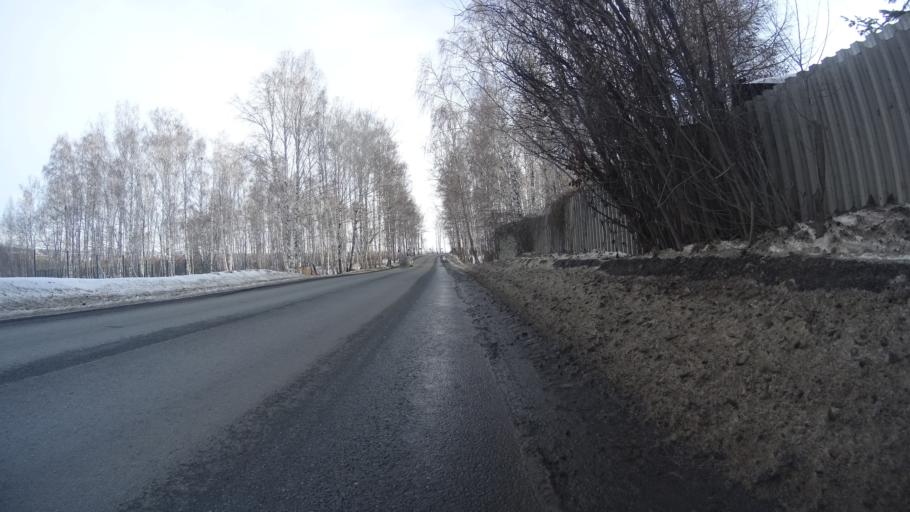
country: RU
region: Chelyabinsk
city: Sargazy
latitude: 55.1269
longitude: 61.2887
